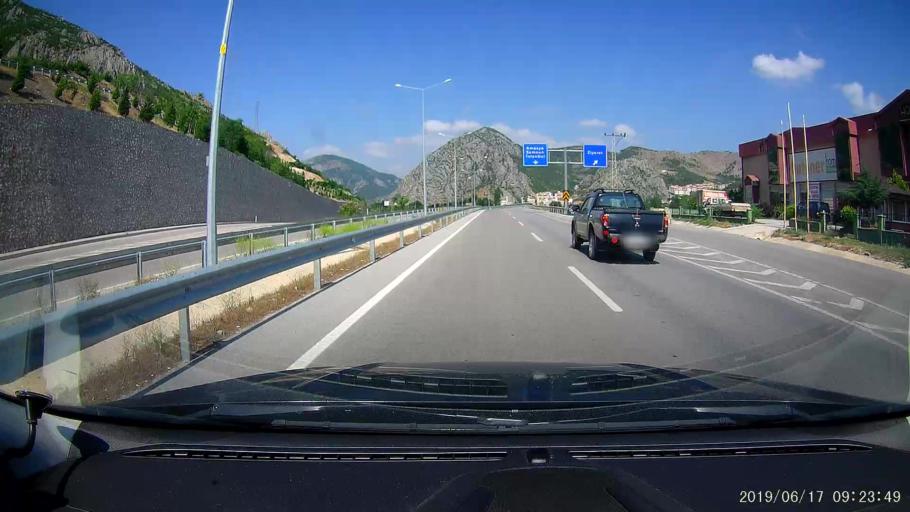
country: TR
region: Amasya
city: Amasya
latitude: 40.6743
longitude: 35.8670
